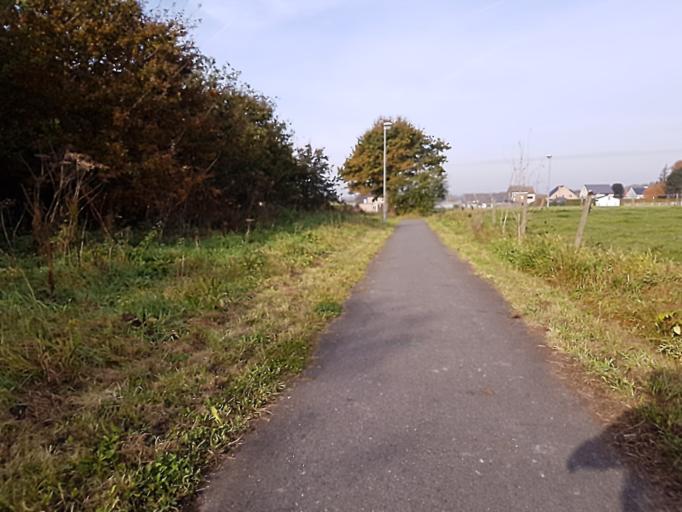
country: BE
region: Flanders
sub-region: Provincie Antwerpen
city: Sint-Katelijne-Waver
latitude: 51.0676
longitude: 4.5708
